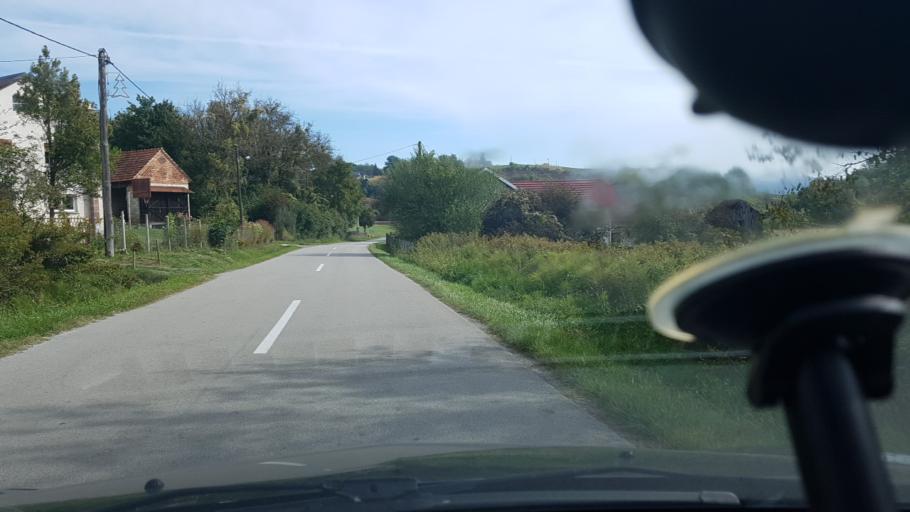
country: HR
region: Varazdinska
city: Remetinec
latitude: 46.1121
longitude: 16.2418
